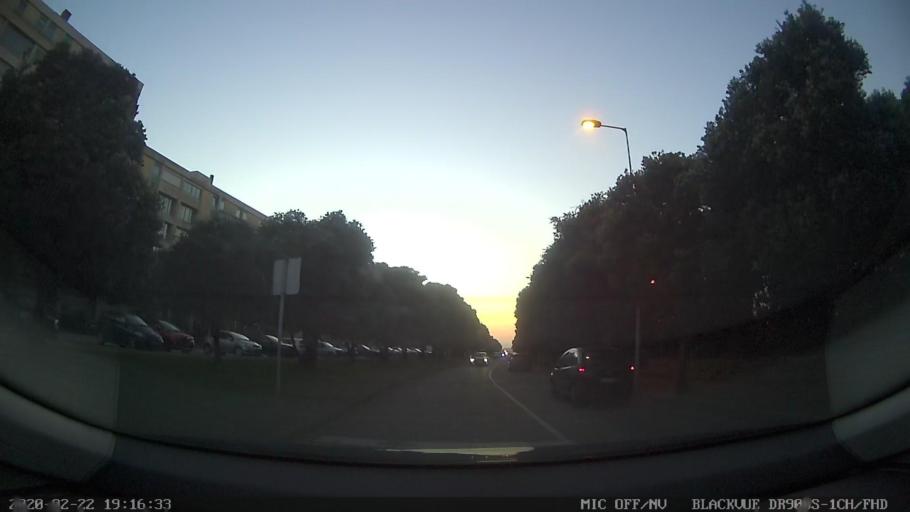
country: PT
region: Porto
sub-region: Matosinhos
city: Leca da Palmeira
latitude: 41.2012
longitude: -8.7039
